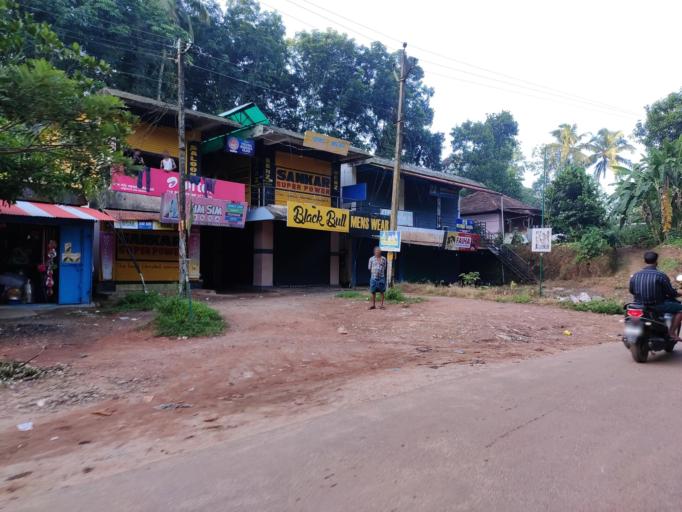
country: IN
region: Kerala
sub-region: Palakkad district
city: Mannarakkat
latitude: 10.9443
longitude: 76.4825
